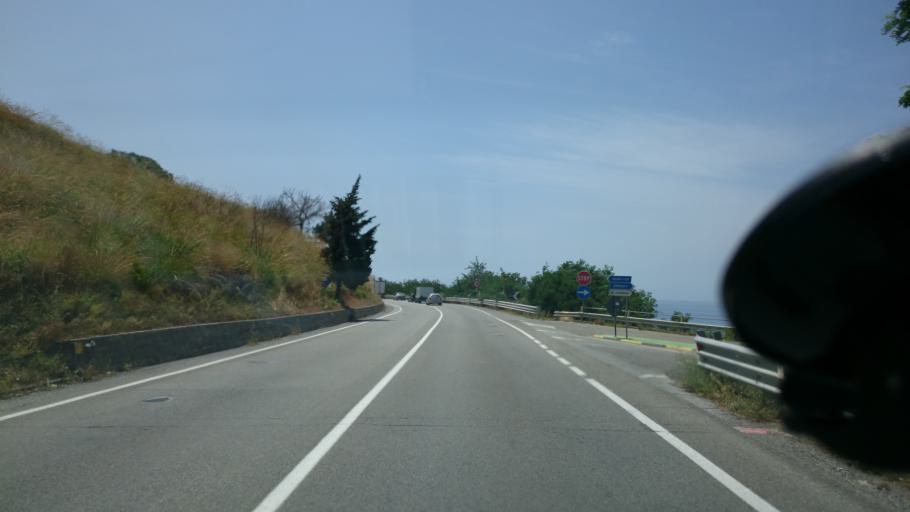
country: IT
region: Calabria
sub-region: Provincia di Cosenza
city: Cittadella del Capo
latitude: 39.5514
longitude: 15.8812
